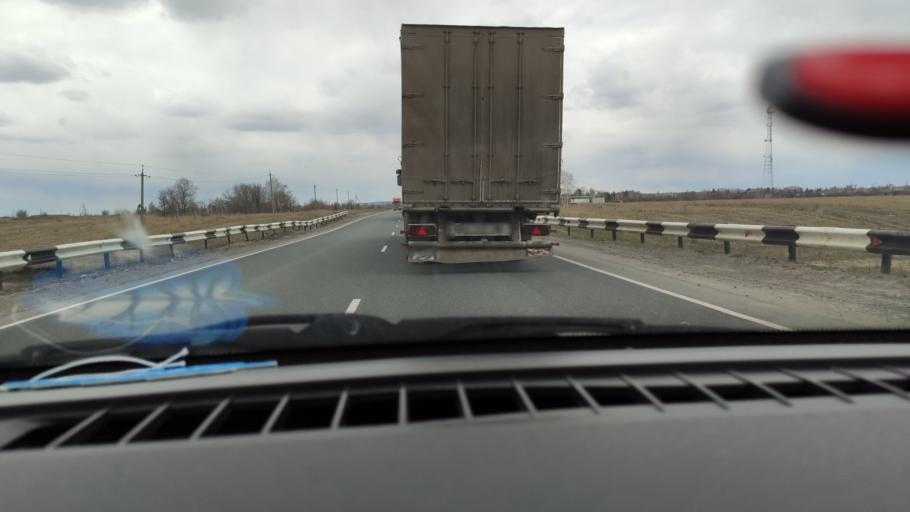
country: RU
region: Saratov
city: Sennoy
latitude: 52.1504
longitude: 46.9776
